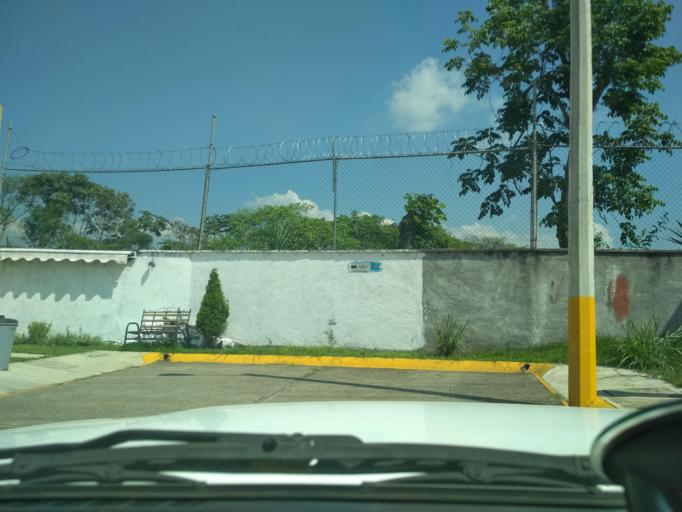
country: MX
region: Veracruz
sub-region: Fortin
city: Fraccionamiento Villas de la Llave
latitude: 18.9152
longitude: -96.9862
